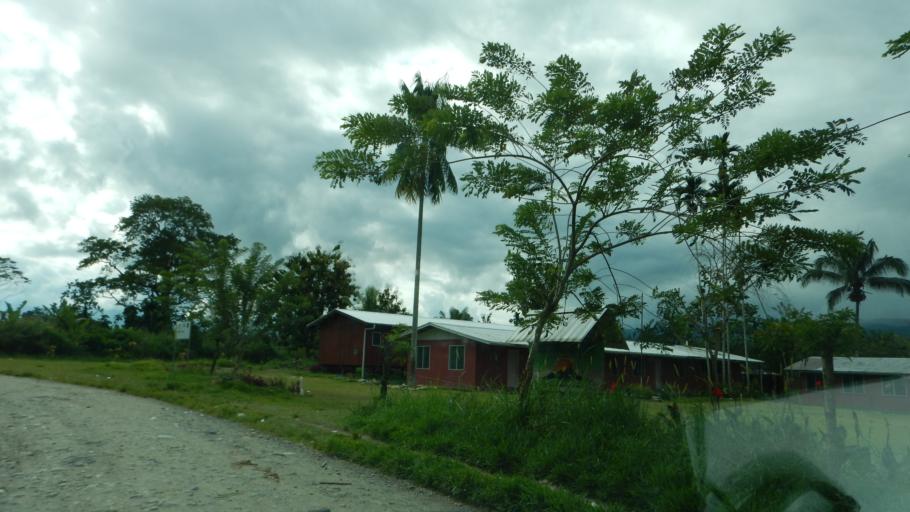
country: PG
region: Northern Province
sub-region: Sohe
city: Kokoda
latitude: -8.8773
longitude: 147.7378
